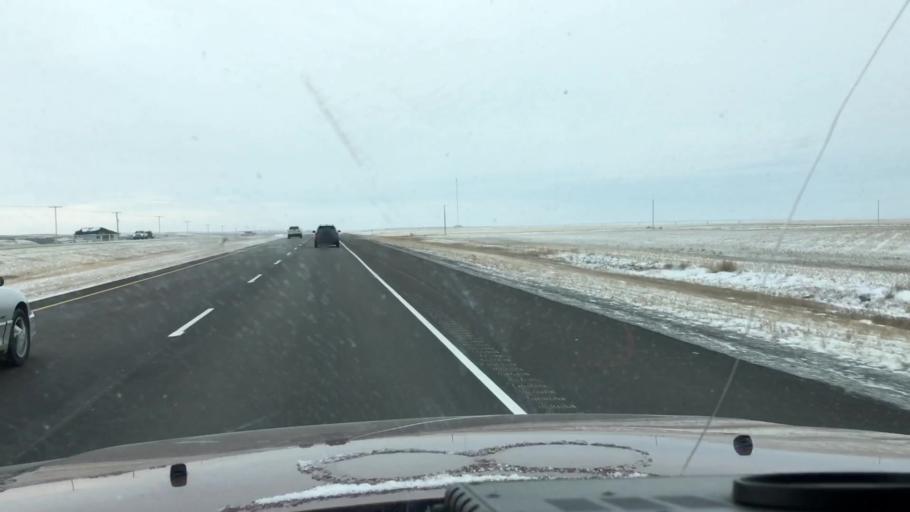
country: CA
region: Saskatchewan
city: Saskatoon
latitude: 51.7532
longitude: -106.4764
